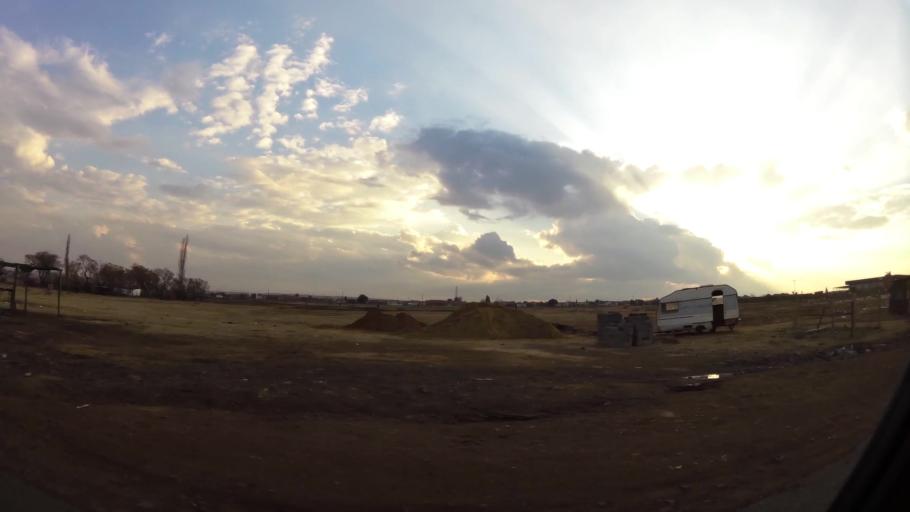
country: ZA
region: Gauteng
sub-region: City of Johannesburg Metropolitan Municipality
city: Orange Farm
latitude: -26.5399
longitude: 27.8325
